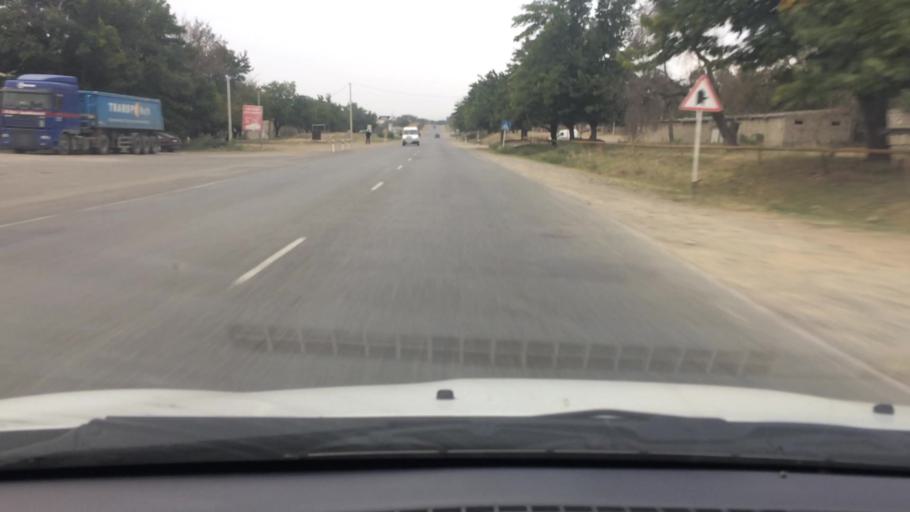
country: GE
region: T'bilisi
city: Tbilisi
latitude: 41.6425
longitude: 44.8376
